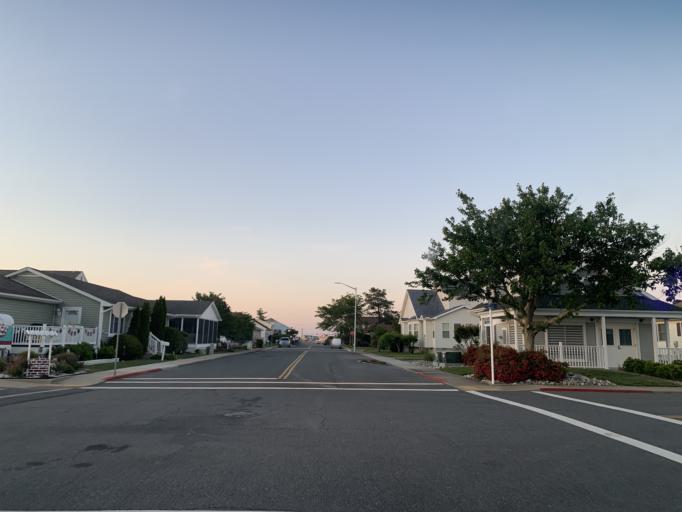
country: US
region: Delaware
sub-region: Sussex County
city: Bethany Beach
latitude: 38.4494
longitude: -75.0642
